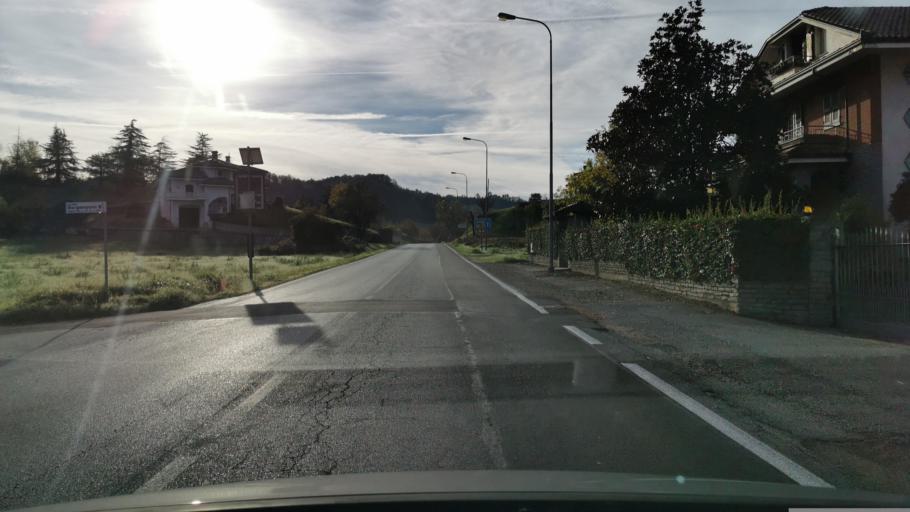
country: IT
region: Piedmont
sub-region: Provincia di Cuneo
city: Monchiero Borgonuovo
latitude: 44.5656
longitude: 7.9203
